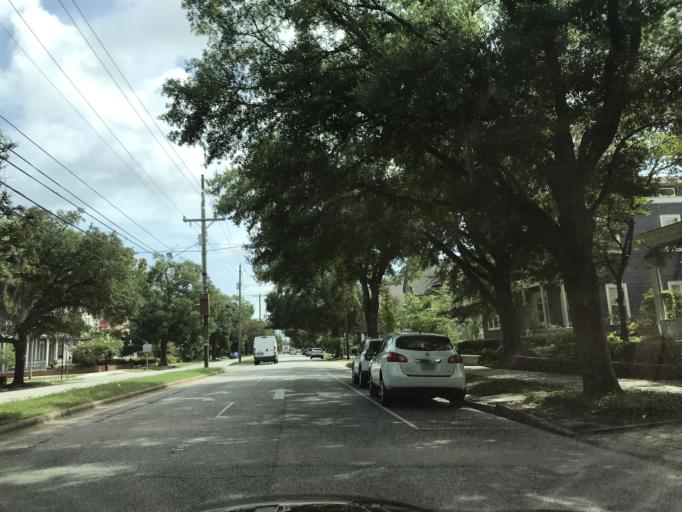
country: US
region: North Carolina
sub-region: New Hanover County
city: Wilmington
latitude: 34.2311
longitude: -77.9456
